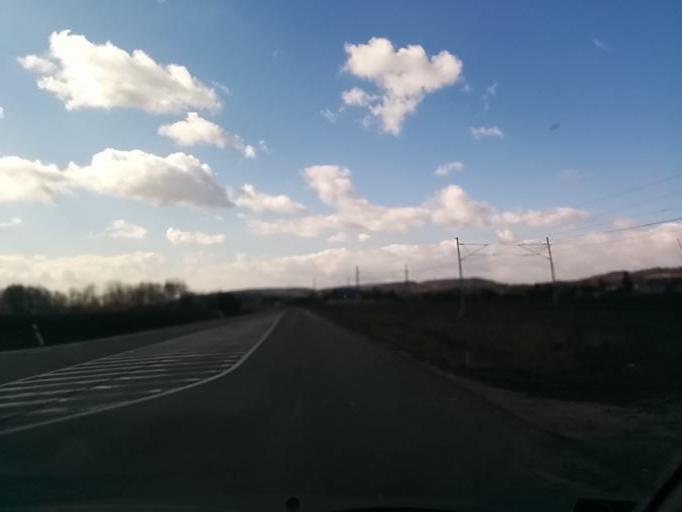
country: SK
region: Trenciansky
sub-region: Okres Nove Mesto nad Vahom
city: Nove Mesto nad Vahom
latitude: 48.8344
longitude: 17.9160
